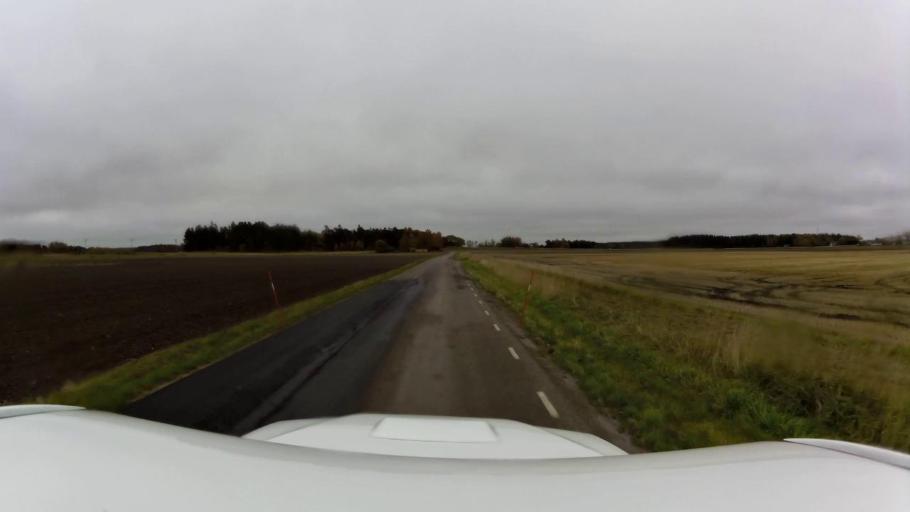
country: SE
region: OEstergoetland
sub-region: Linkopings Kommun
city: Linghem
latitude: 58.4355
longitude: 15.7165
